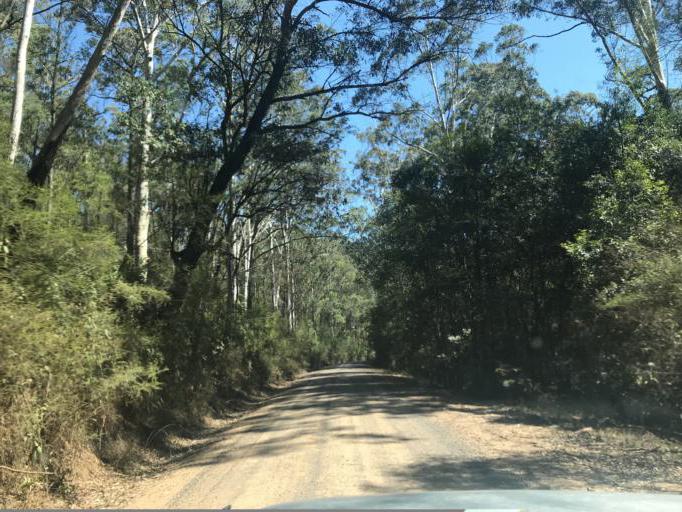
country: AU
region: New South Wales
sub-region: Wyong Shire
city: Little Jilliby
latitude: -33.1795
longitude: 151.0623
